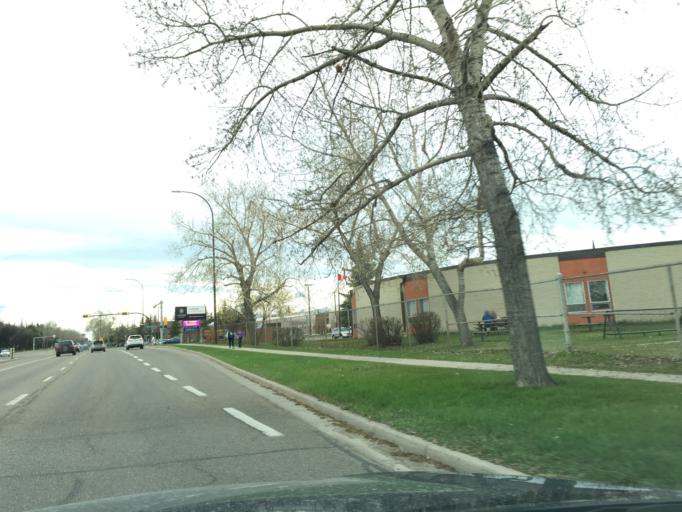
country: CA
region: Alberta
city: Calgary
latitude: 50.9615
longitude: -114.1049
